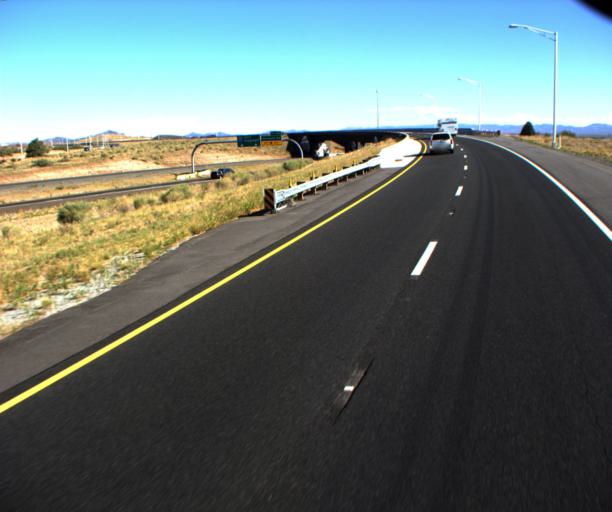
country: US
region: Arizona
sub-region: Yavapai County
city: Cordes Lakes
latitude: 34.3264
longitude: -112.1207
